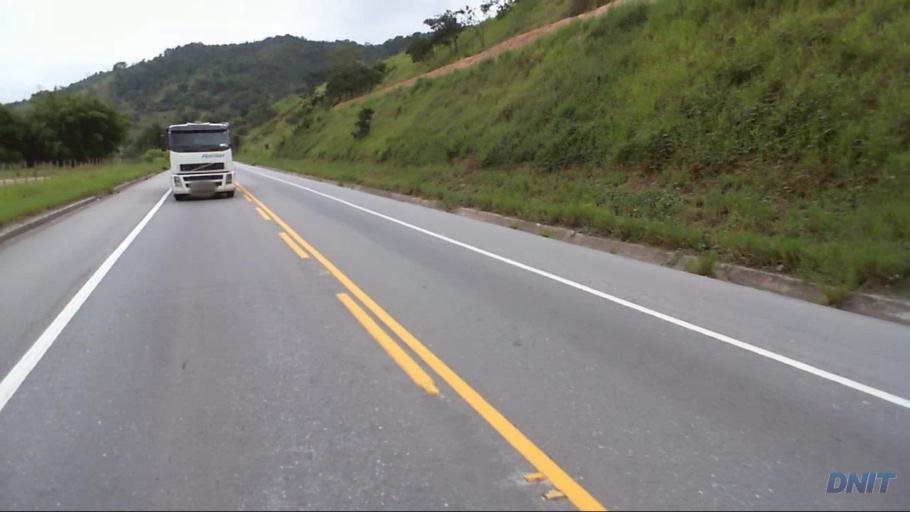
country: BR
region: Minas Gerais
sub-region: Nova Era
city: Nova Era
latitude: -19.7181
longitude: -43.0031
